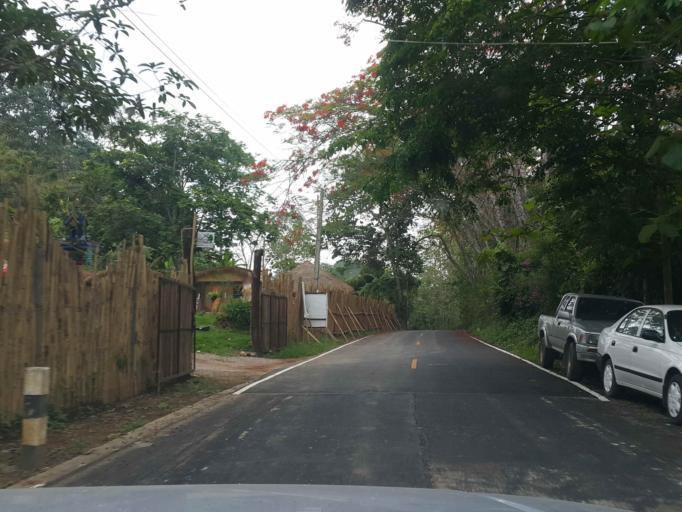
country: TH
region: Chiang Mai
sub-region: Amphoe Chiang Dao
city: Chiang Dao
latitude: 19.4097
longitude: 98.9230
